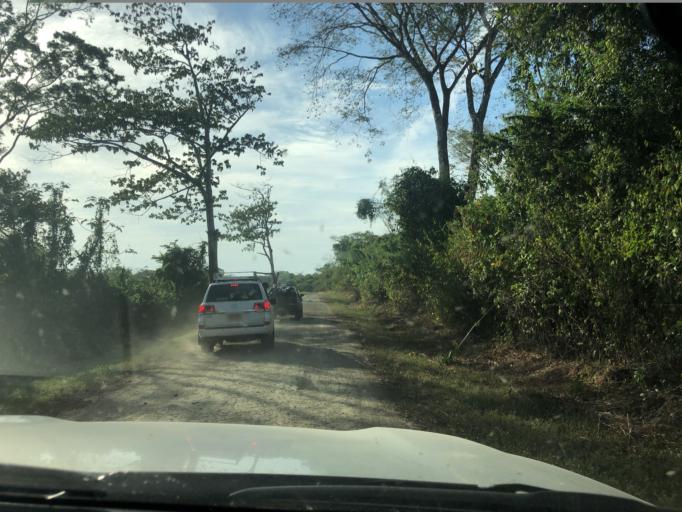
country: NI
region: Rivas
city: Cardenas
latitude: 11.1249
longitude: -85.2921
